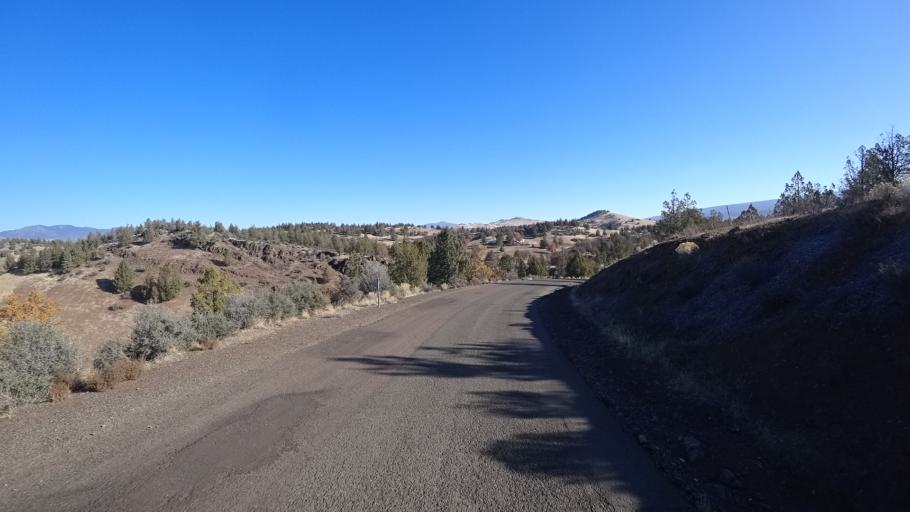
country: US
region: California
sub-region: Siskiyou County
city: Montague
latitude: 41.9109
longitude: -122.4365
